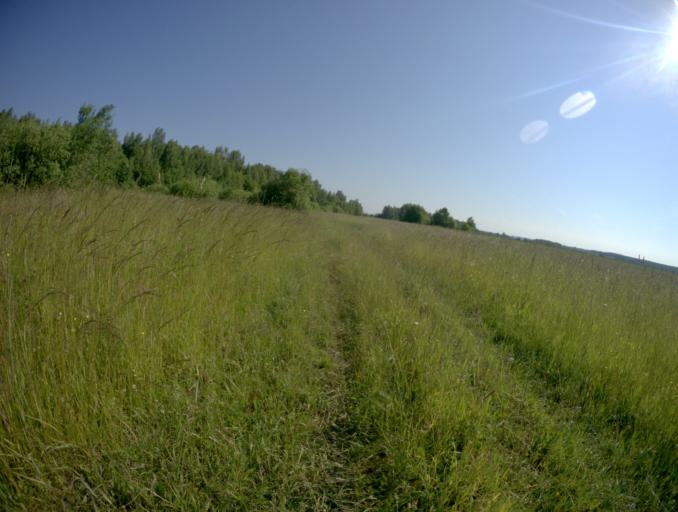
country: RU
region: Vladimir
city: Novovyazniki
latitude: 56.1937
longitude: 42.1921
